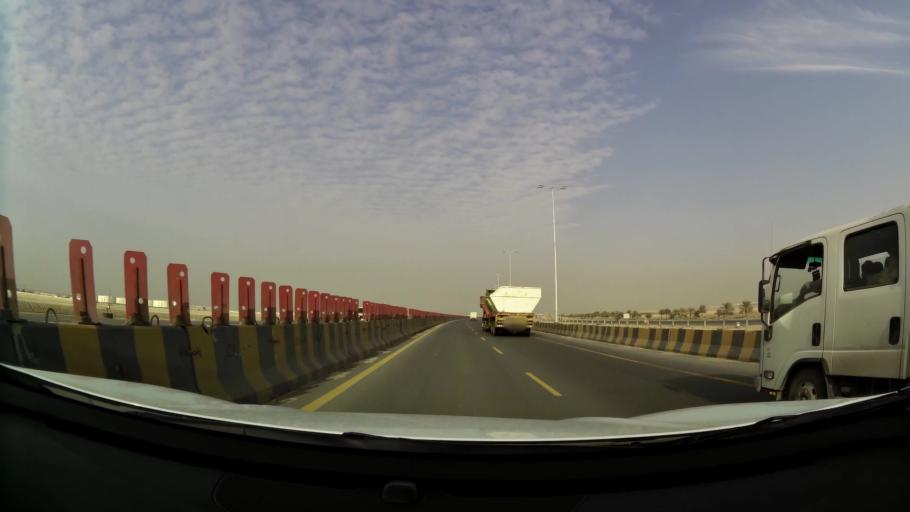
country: AE
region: Abu Dhabi
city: Abu Dhabi
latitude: 24.2687
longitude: 54.4979
